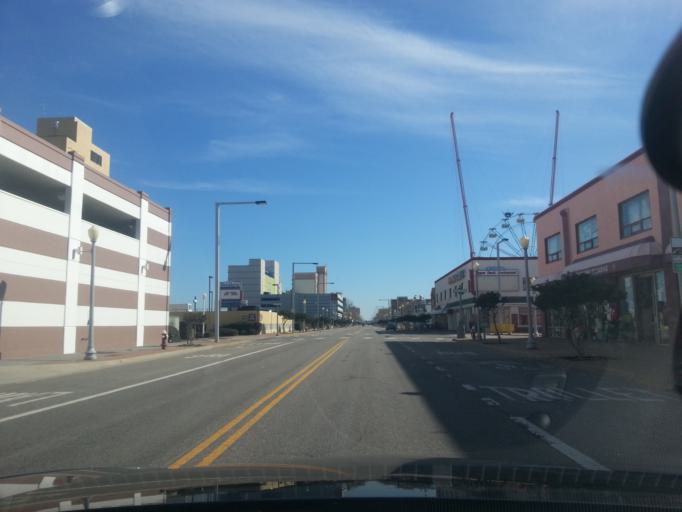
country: US
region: Virginia
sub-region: City of Virginia Beach
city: Virginia Beach
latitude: 36.8449
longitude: -75.9741
